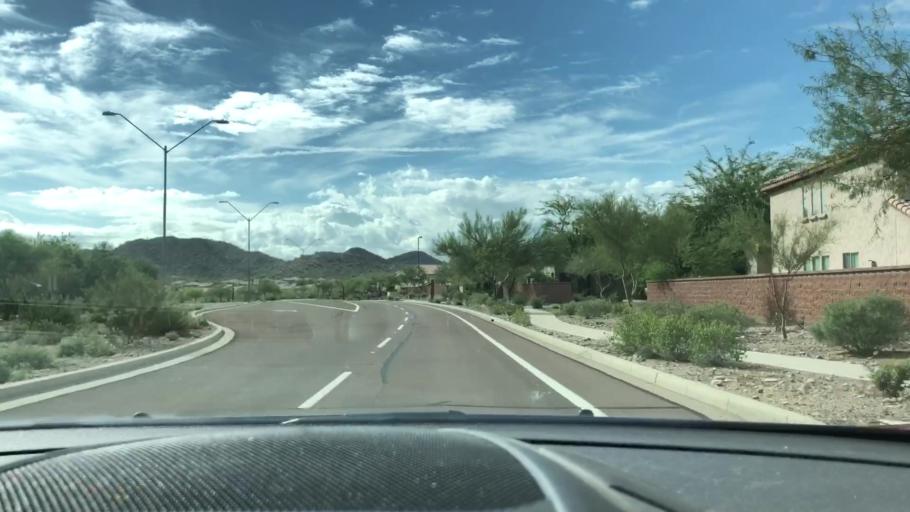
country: US
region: Arizona
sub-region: Maricopa County
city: Sun City West
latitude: 33.7335
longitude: -112.2538
